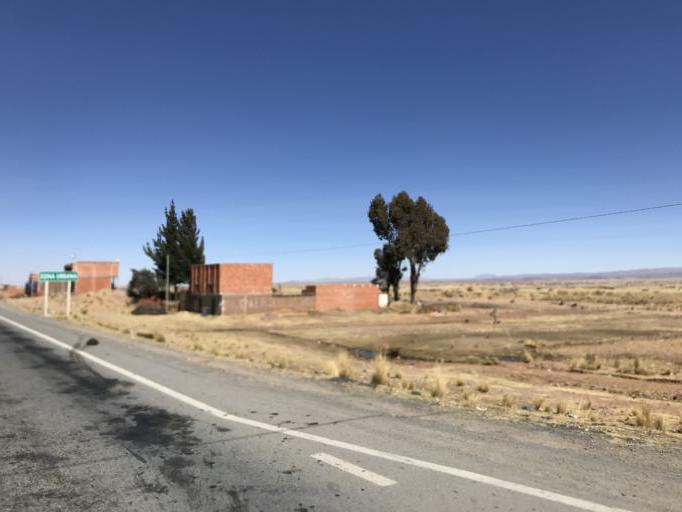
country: BO
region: La Paz
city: Batallas
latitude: -16.3974
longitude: -68.3619
